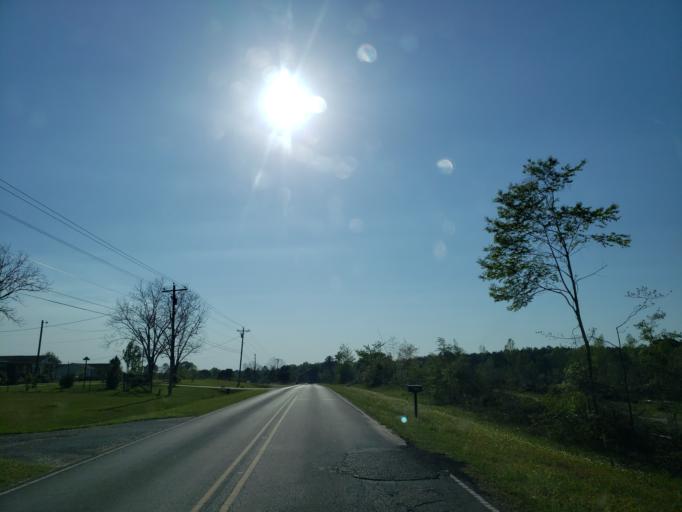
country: US
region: Mississippi
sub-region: Perry County
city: Richton
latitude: 31.4823
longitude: -89.0191
